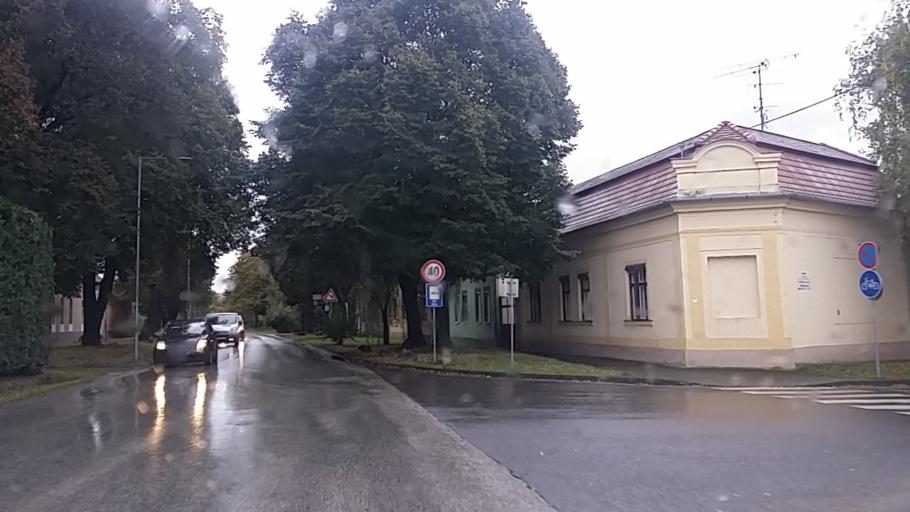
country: SK
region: Nitriansky
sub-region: Okres Nove Zamky
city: Sturovo
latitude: 47.8013
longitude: 18.7236
